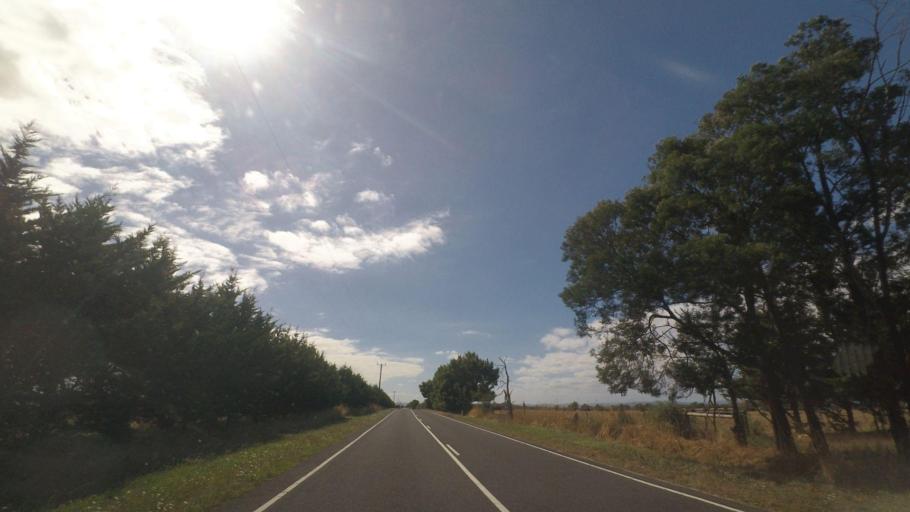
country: AU
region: Victoria
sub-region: Cardinia
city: Garfield
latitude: -38.2086
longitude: 145.6343
